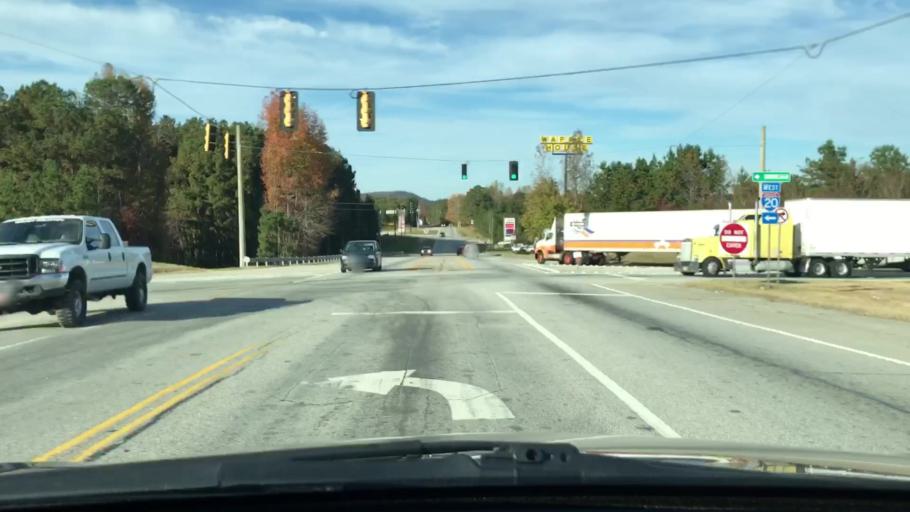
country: US
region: Georgia
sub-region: Haralson County
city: Tallapoosa
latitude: 33.6853
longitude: -85.2621
